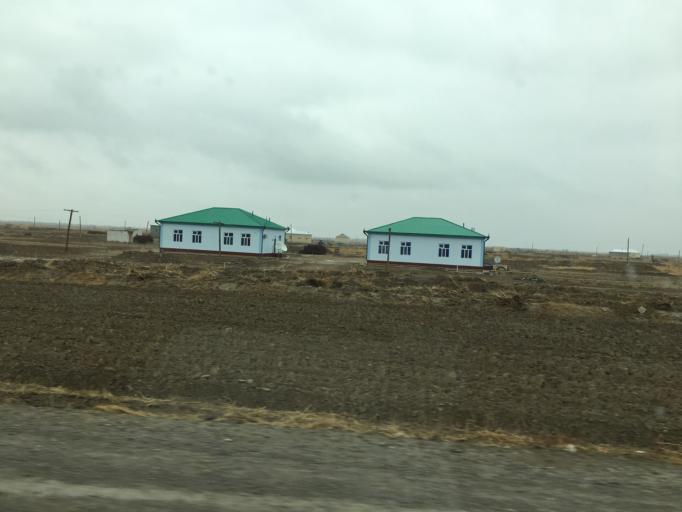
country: TM
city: Murgab
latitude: 37.4728
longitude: 62.0238
